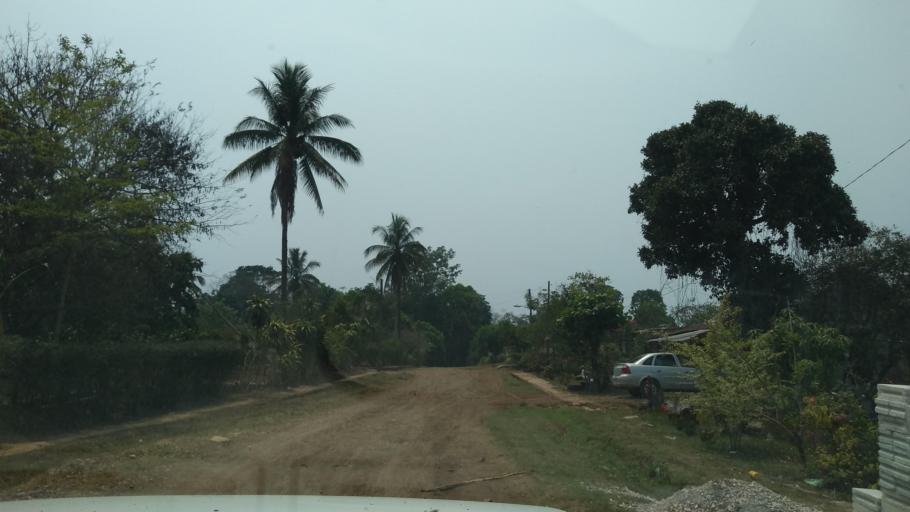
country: MX
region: Veracruz
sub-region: Tezonapa
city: Laguna Chica (Pueblo Nuevo)
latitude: 18.5329
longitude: -96.7632
